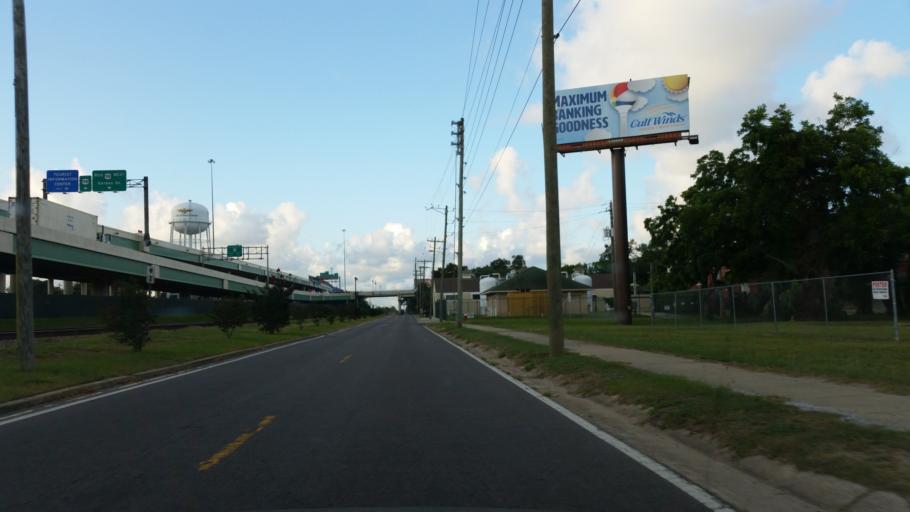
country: US
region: Florida
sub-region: Escambia County
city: Pensacola
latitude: 30.4245
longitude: -87.2154
